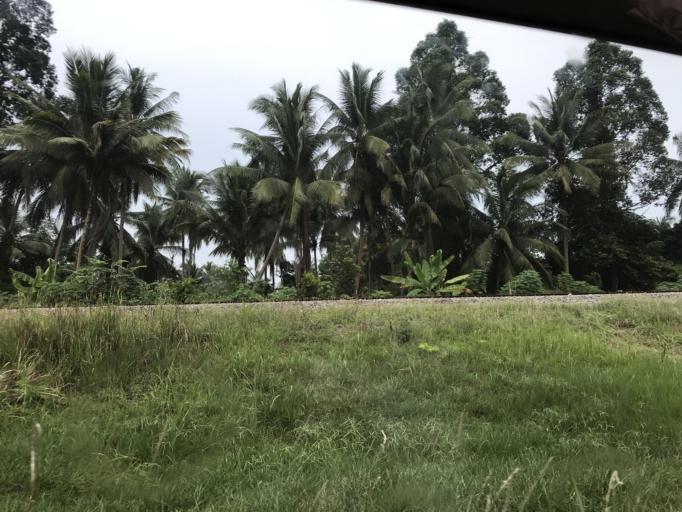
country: MY
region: Kelantan
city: Tumpat
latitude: 6.1656
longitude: 102.2004
